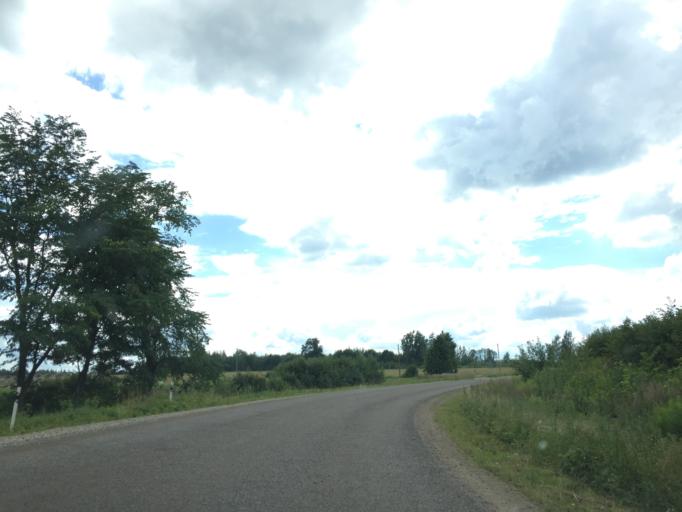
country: LV
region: Sigulda
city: Sigulda
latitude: 57.1824
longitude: 24.9356
